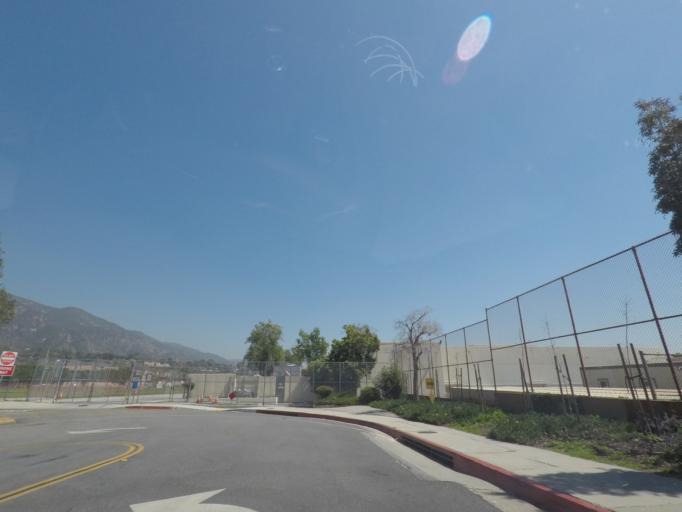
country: US
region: California
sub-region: Los Angeles County
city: East Pasadena
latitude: 34.1630
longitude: -118.0942
